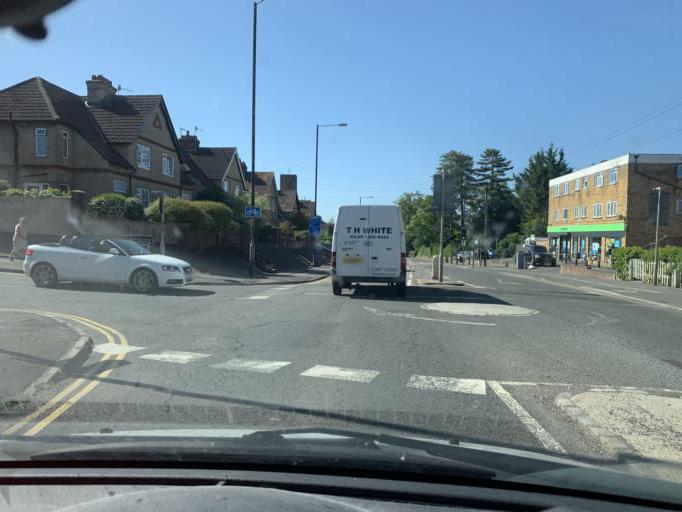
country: GB
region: England
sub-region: Wiltshire
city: Salisbury
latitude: 51.0841
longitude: -1.7974
